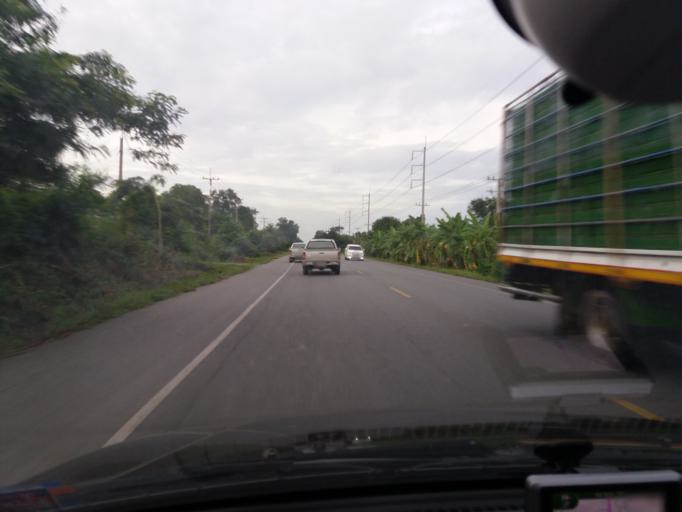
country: TH
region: Suphan Buri
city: U Thong
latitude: 14.5041
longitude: 99.9178
